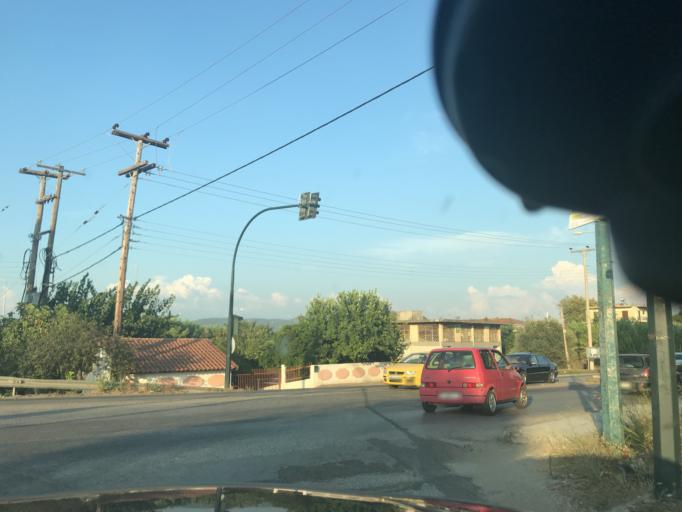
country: GR
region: West Greece
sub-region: Nomos Ileias
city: Pyrgos
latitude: 37.6809
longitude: 21.4216
